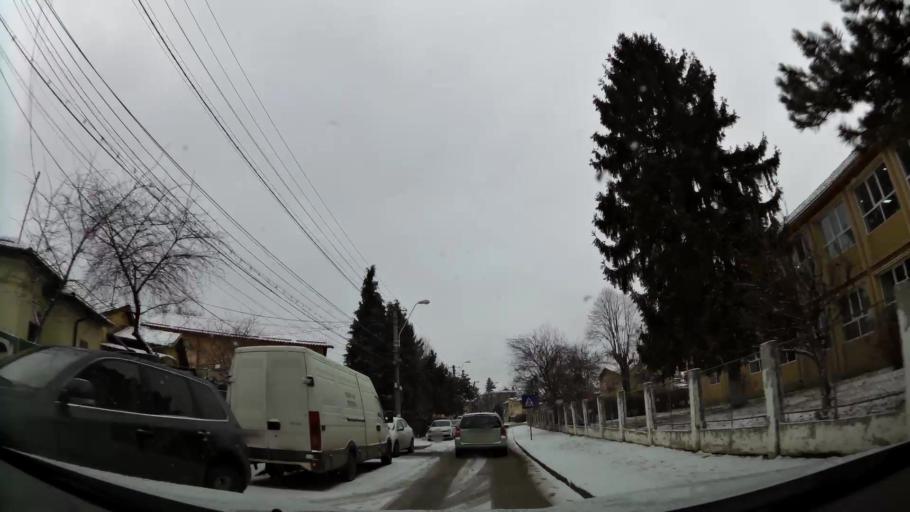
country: RO
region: Prahova
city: Ploiesti
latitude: 44.9361
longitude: 26.0335
